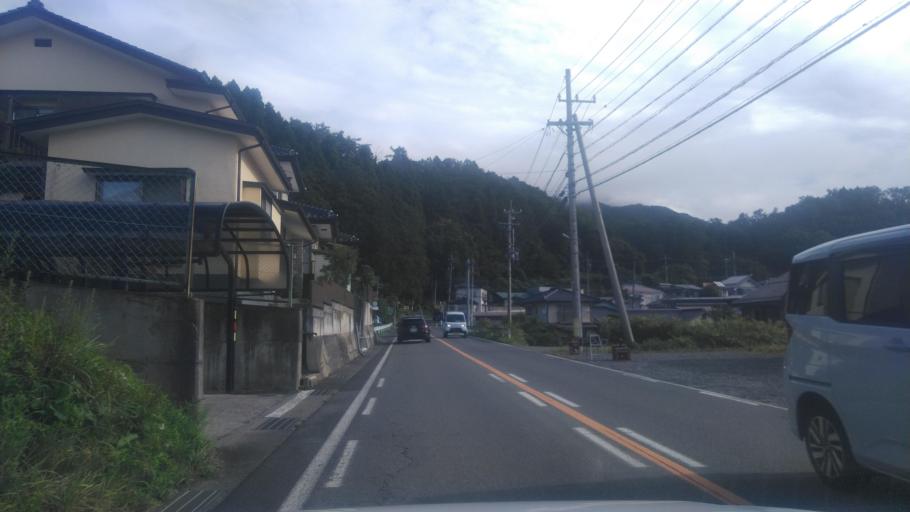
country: JP
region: Nagano
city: Nagano-shi
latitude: 36.6849
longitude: 138.2062
